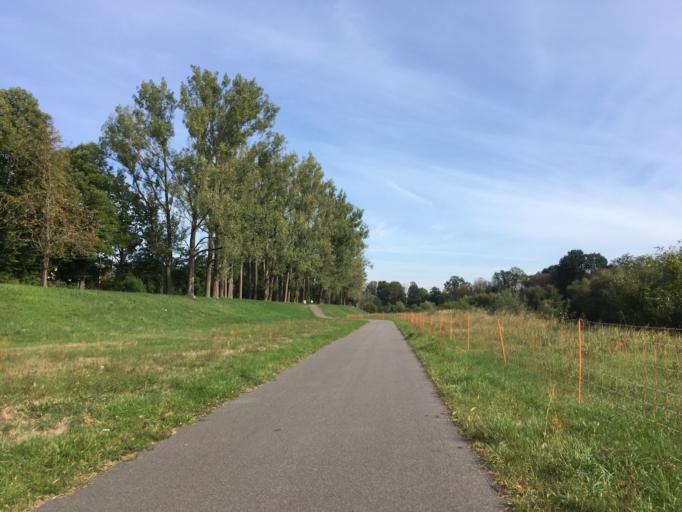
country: DE
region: Brandenburg
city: Forst
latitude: 51.7463
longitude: 14.6587
